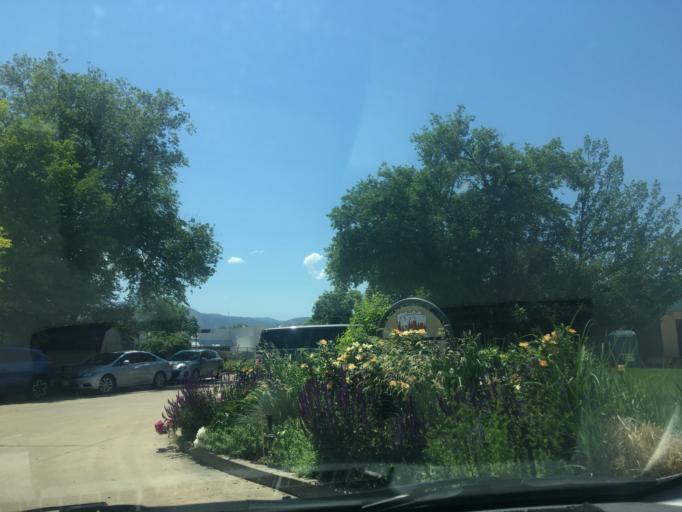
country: US
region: Colorado
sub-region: Boulder County
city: Boulder
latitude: 40.0159
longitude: -105.2099
